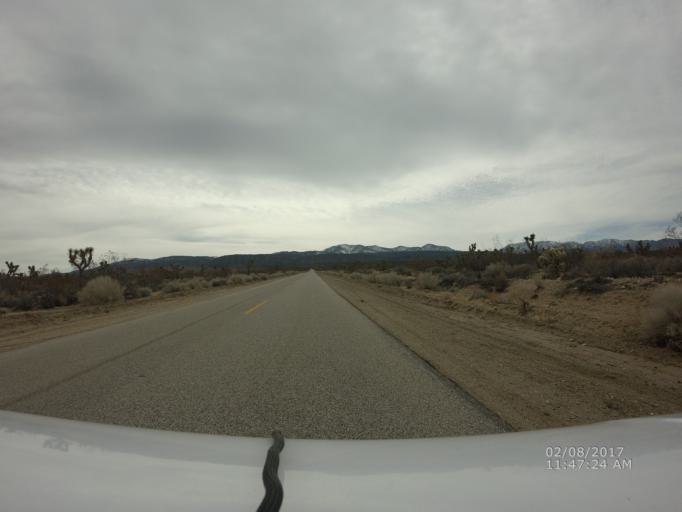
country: US
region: California
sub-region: San Bernardino County
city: Pinon Hills
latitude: 34.4873
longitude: -117.7481
